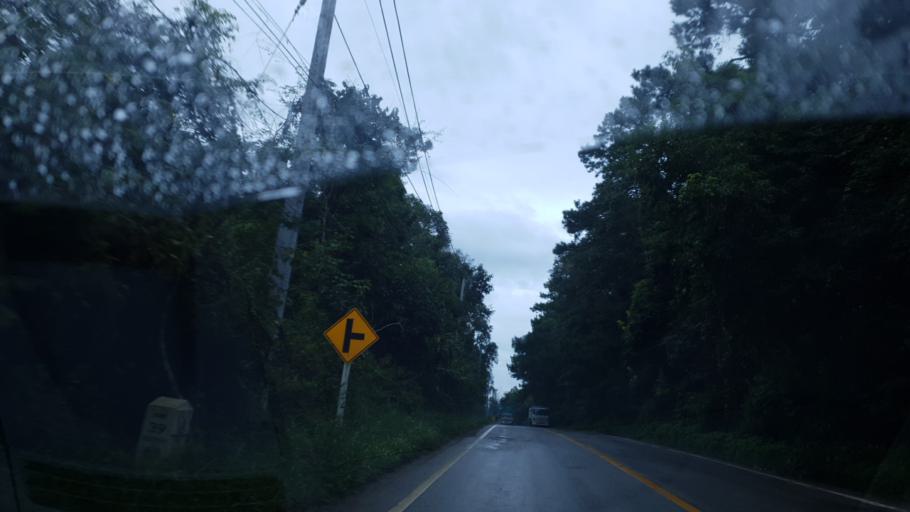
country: TH
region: Chiang Mai
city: Hot
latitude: 18.1413
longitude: 98.3697
